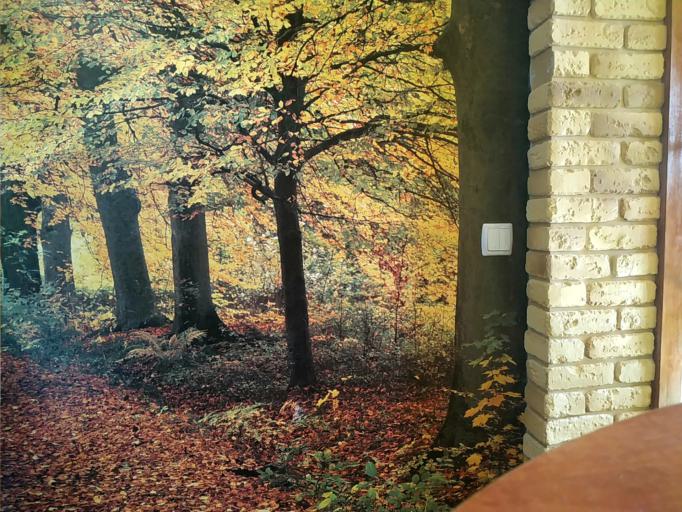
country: RU
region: Jaroslavl
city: Kukoboy
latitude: 58.8475
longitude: 39.7405
